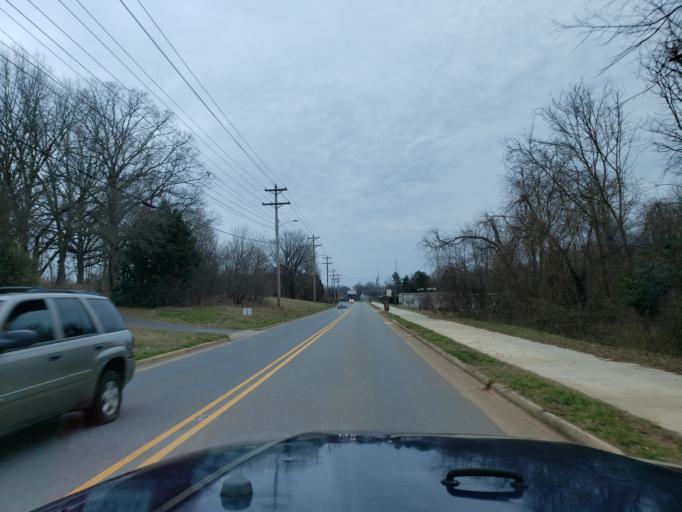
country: US
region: North Carolina
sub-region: Cleveland County
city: Shelby
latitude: 35.3024
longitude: -81.5519
